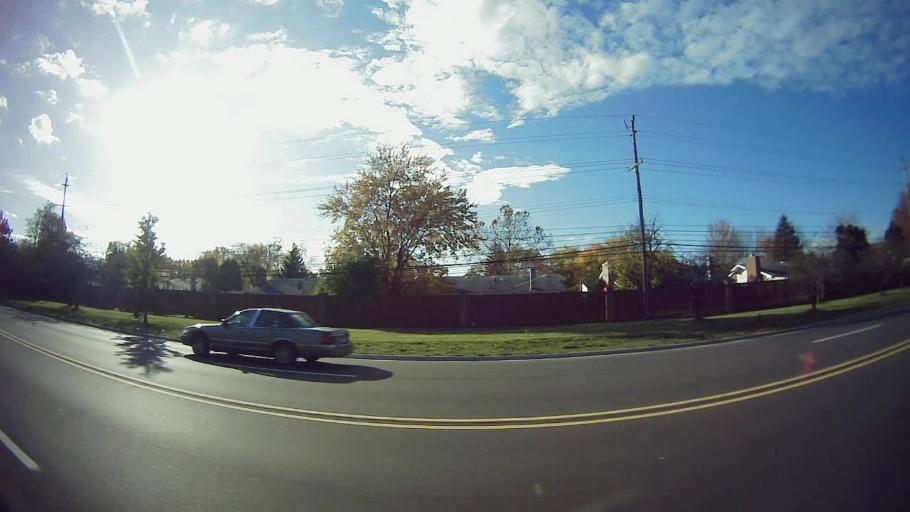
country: US
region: Michigan
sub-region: Oakland County
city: Lathrup Village
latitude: 42.4928
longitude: -83.2414
